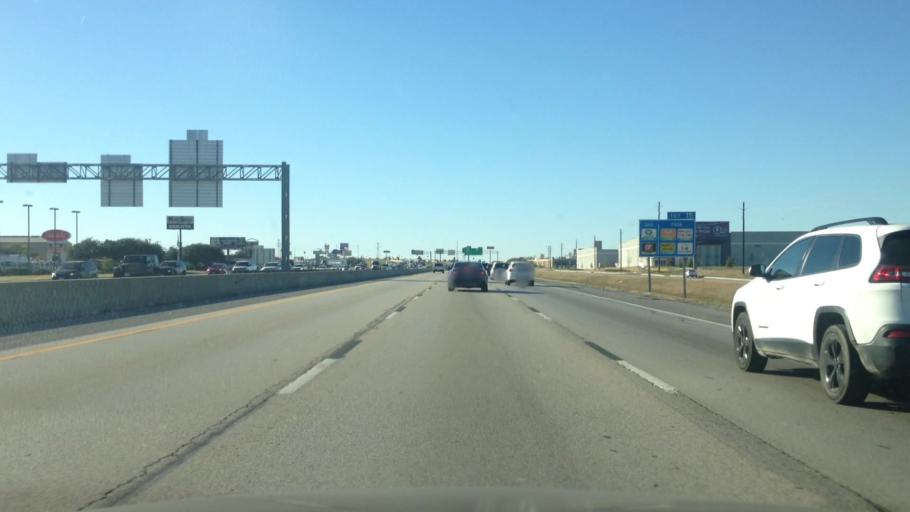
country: US
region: Texas
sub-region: Tarrant County
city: Blue Mound
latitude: 32.8411
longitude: -97.3330
